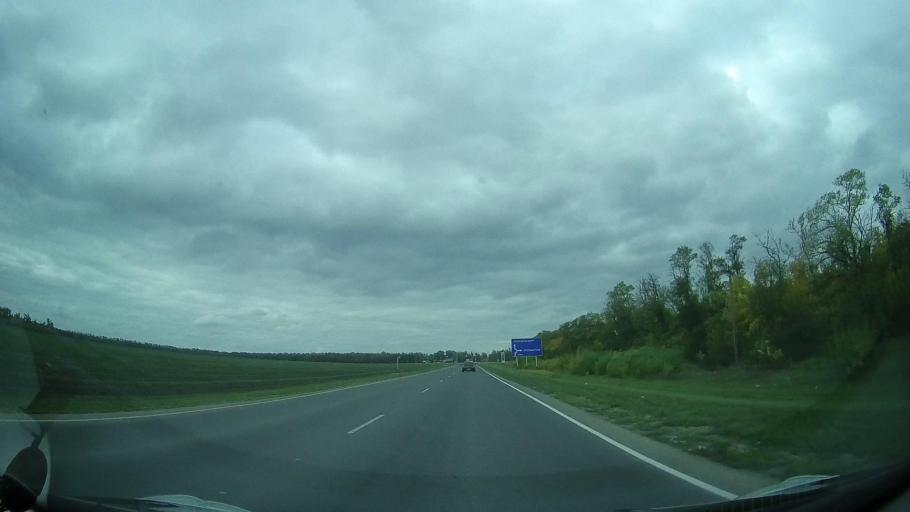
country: RU
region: Rostov
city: Yegorlykskaya
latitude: 46.5812
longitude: 40.6322
